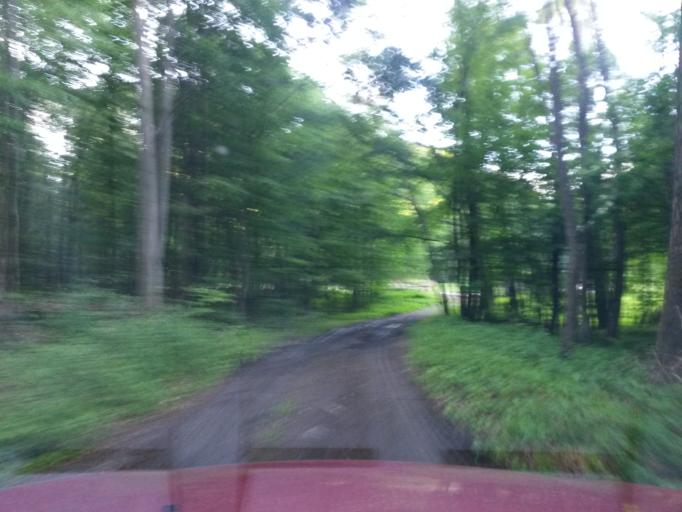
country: SK
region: Kosicky
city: Moldava nad Bodvou
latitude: 48.7388
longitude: 21.0637
